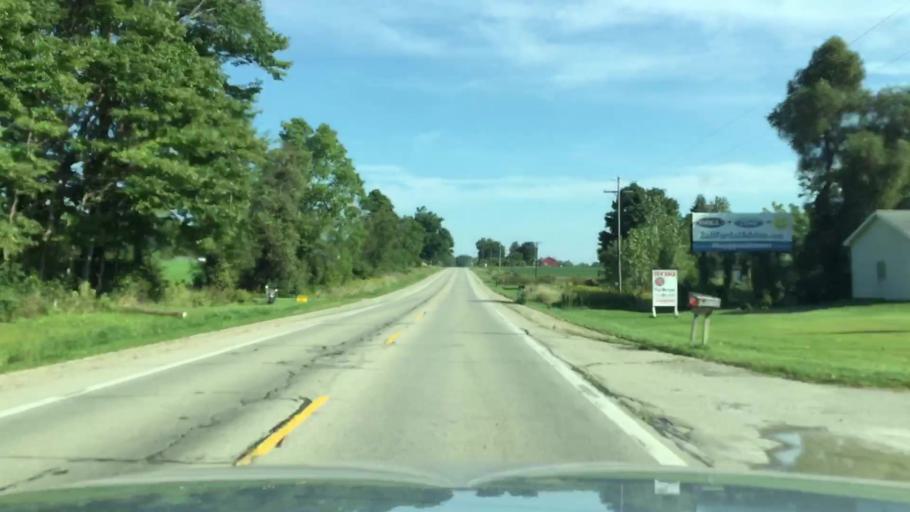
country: US
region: Michigan
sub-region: Lenawee County
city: Manitou Beach-Devils Lake
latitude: 41.9521
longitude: -84.3671
